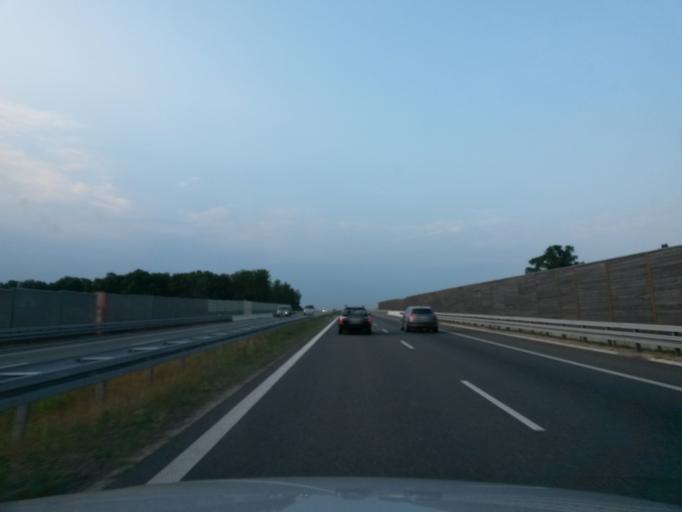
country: PL
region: Lower Silesian Voivodeship
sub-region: Powiat olesnicki
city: Twardogora
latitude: 51.2646
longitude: 17.5492
